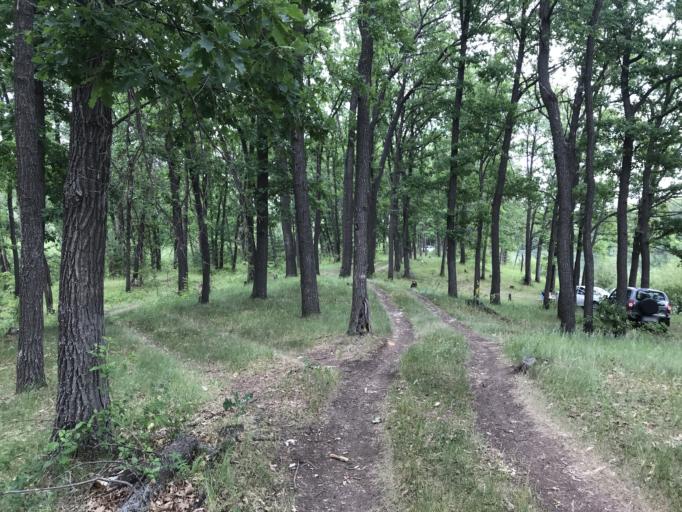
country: RU
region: Samara
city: Pribrezhnyy
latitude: 53.4681
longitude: 49.8158
